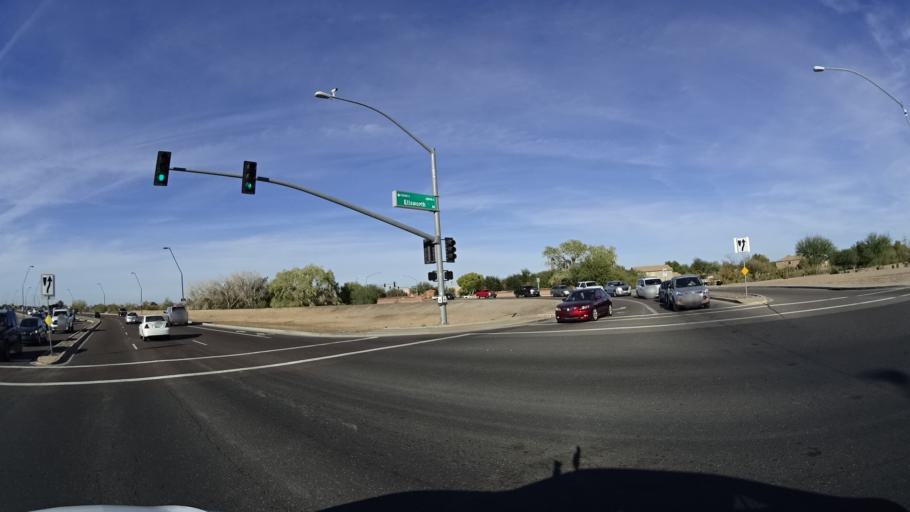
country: US
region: Arizona
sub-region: Maricopa County
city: Queen Creek
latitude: 33.2396
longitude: -111.6349
